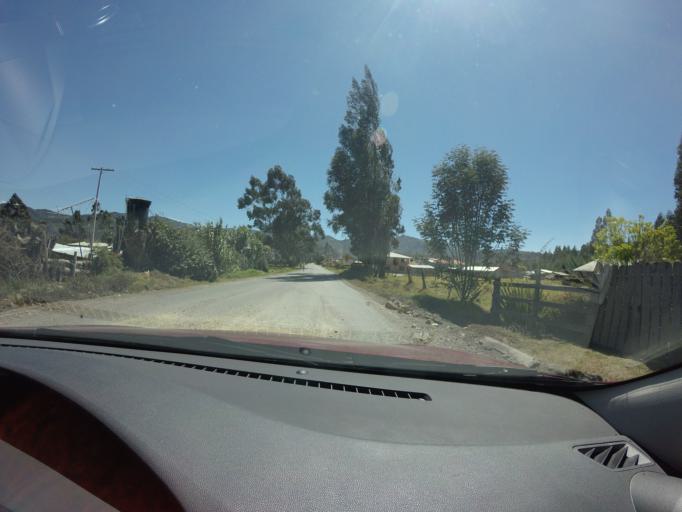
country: CO
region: Cundinamarca
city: Cucunuba
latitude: 5.2625
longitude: -73.7885
